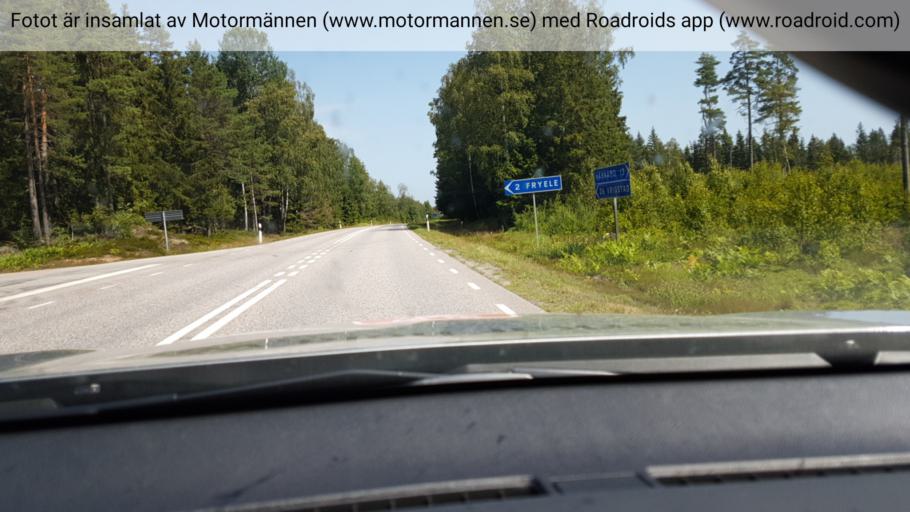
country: SE
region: Joenkoeping
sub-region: Varnamo Kommun
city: Bor
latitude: 57.2544
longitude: 14.1817
